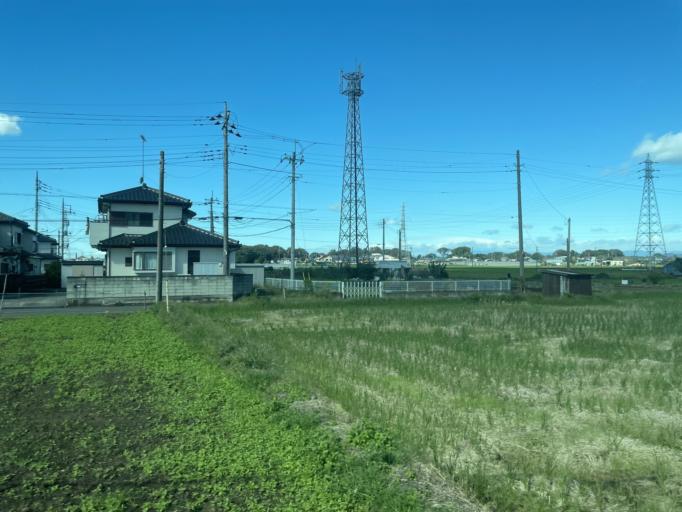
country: JP
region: Ibaraki
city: Koga
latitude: 36.2094
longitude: 139.7158
